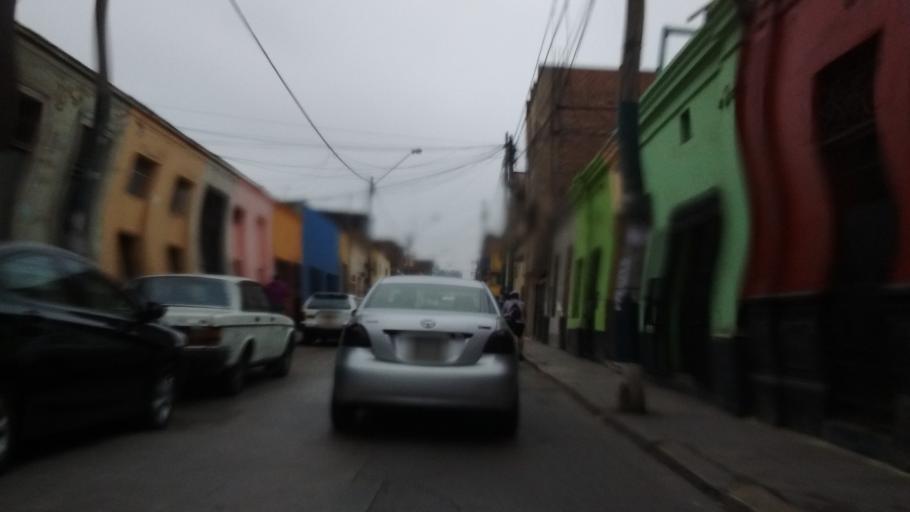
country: PE
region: Lima
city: Lima
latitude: -12.0678
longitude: -77.0279
